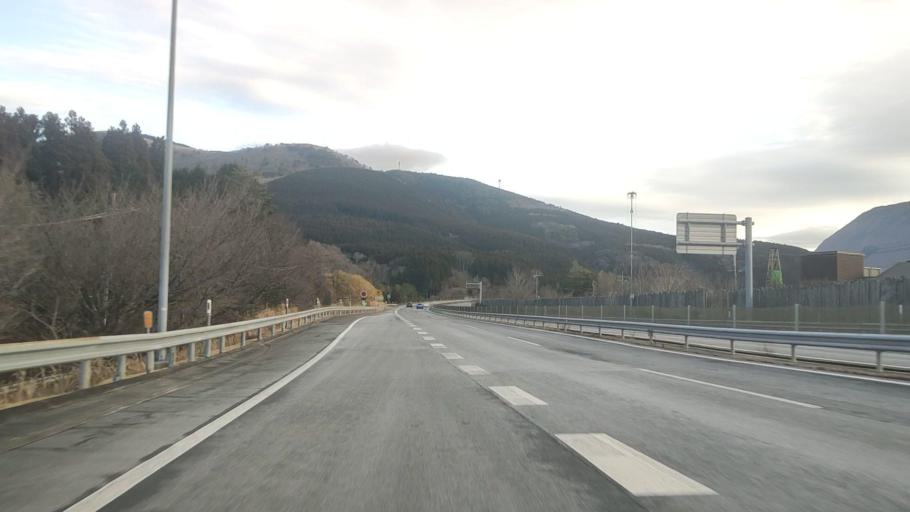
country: JP
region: Oita
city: Beppu
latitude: 33.2598
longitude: 131.3309
